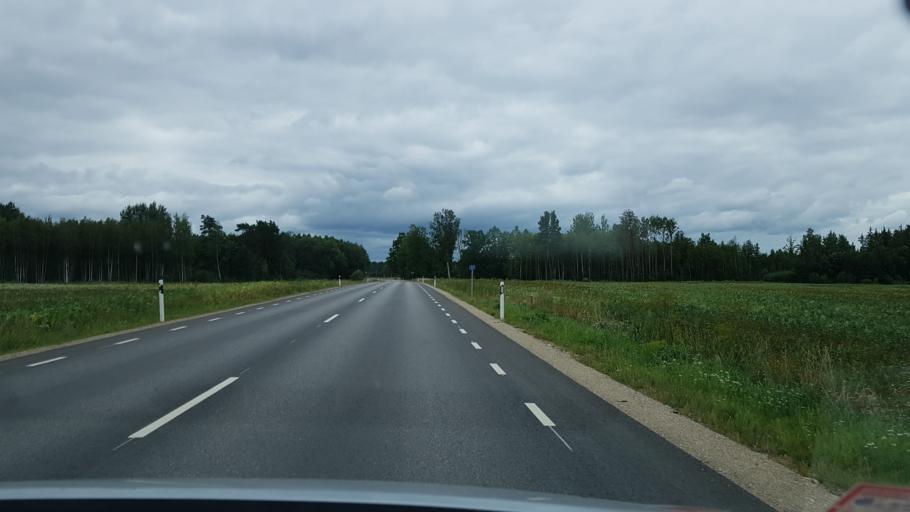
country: EE
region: Polvamaa
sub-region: Polva linn
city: Polva
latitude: 58.0785
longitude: 27.2442
